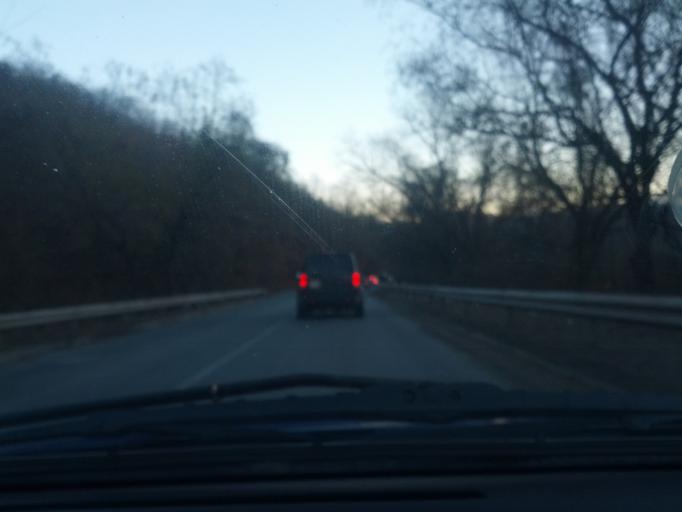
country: BG
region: Vratsa
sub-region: Obshtina Mezdra
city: Mezdra
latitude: 43.0166
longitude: 23.6900
